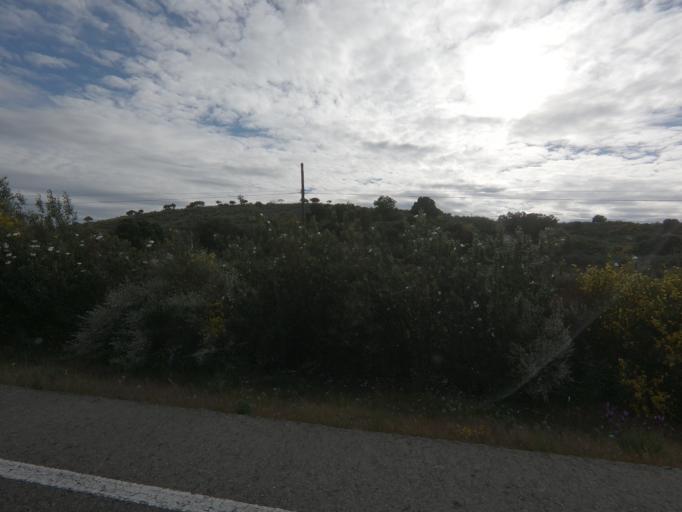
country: ES
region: Extremadura
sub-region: Provincia de Caceres
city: Perales del Puerto
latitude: 40.1184
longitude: -6.6714
